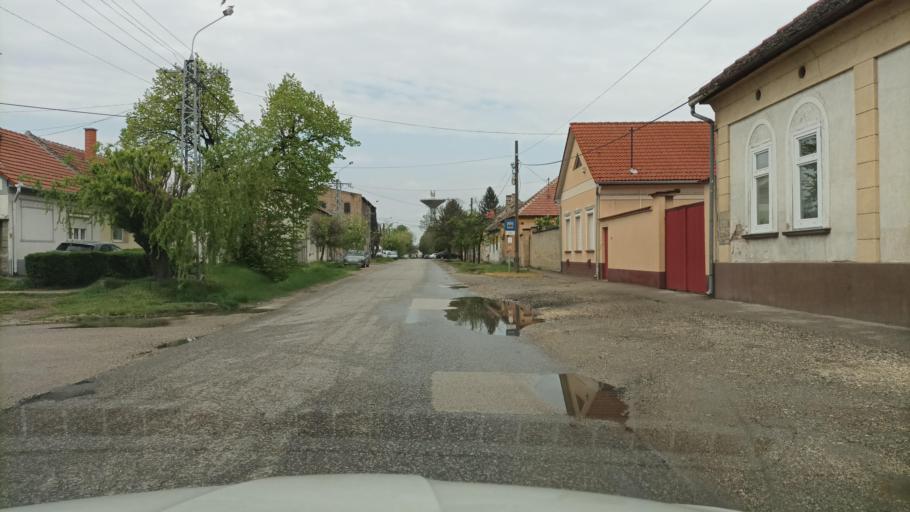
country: HU
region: Pest
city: Nagykoros
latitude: 47.0258
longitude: 19.7875
